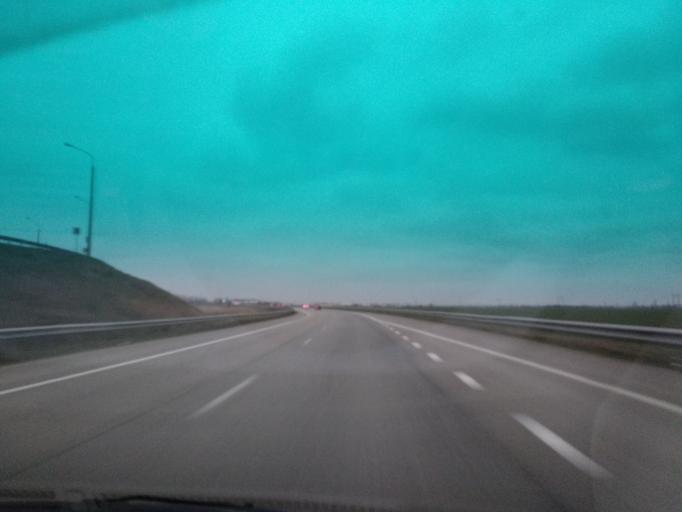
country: RU
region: Adygeya
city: Adygeysk
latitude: 44.8932
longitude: 39.1660
